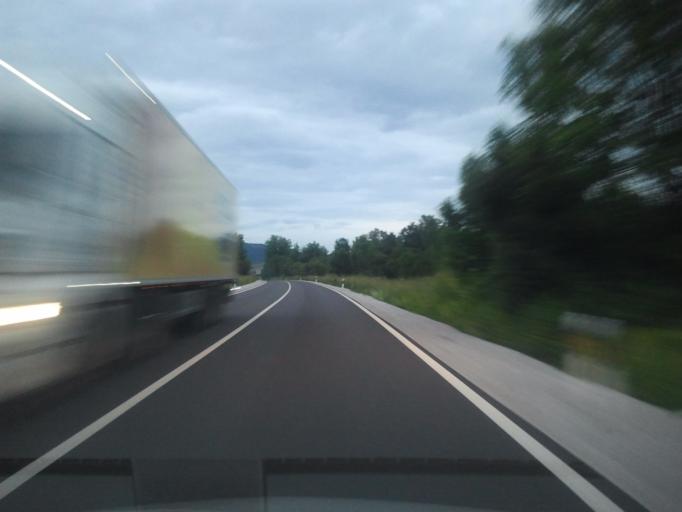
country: HR
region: Zadarska
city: Gracac
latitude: 44.3433
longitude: 15.8674
